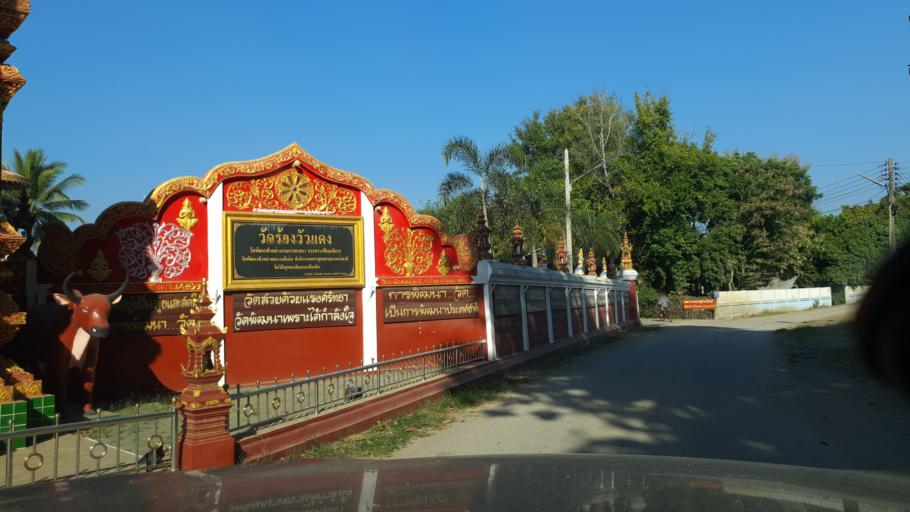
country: TH
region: Chiang Mai
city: San Kamphaeng
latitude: 18.7444
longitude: 99.1716
